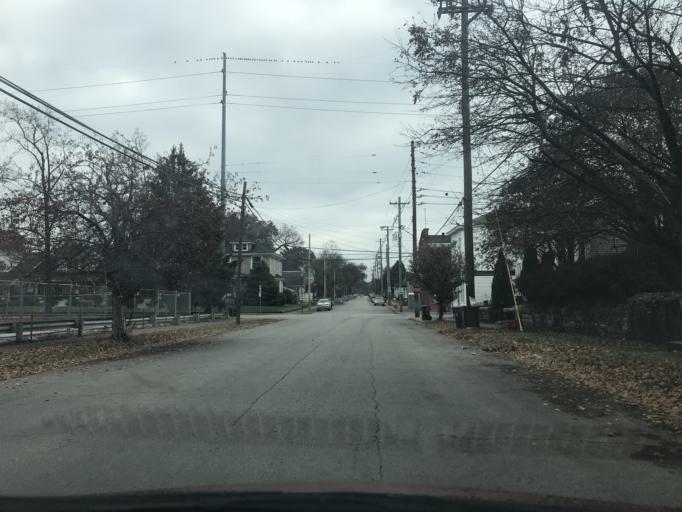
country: US
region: Kentucky
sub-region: Jefferson County
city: Louisville
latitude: 38.2399
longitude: -85.7332
